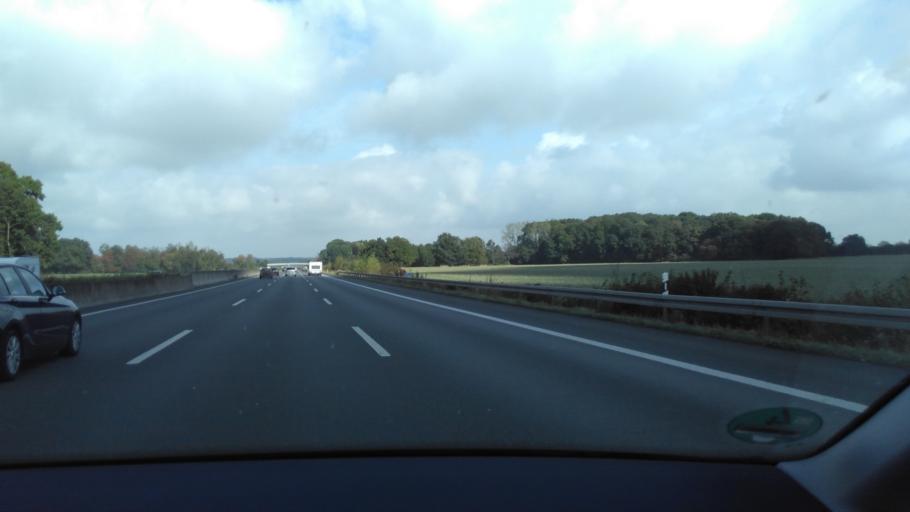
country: DE
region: North Rhine-Westphalia
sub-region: Regierungsbezirk Munster
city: Beckum
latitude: 51.7380
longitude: 7.9885
